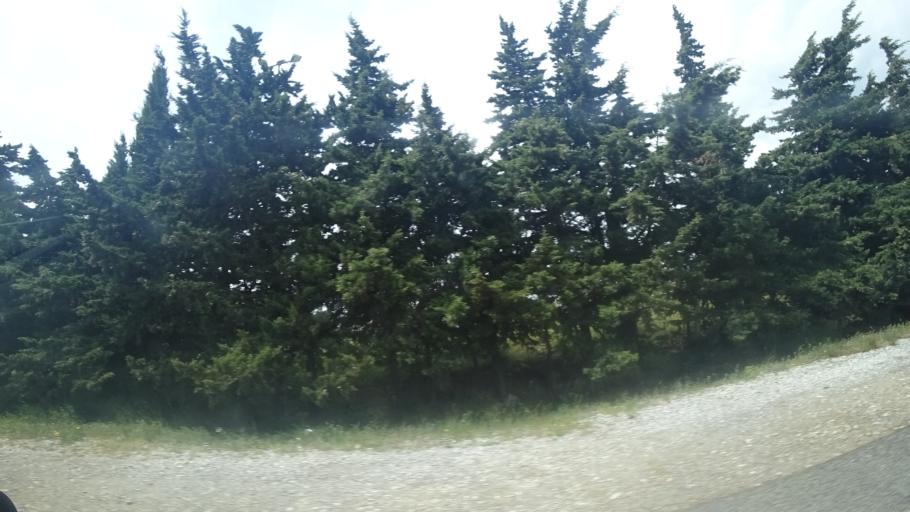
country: FR
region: Languedoc-Roussillon
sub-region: Departement de l'Aude
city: Leucate
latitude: 42.9036
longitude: 3.0342
